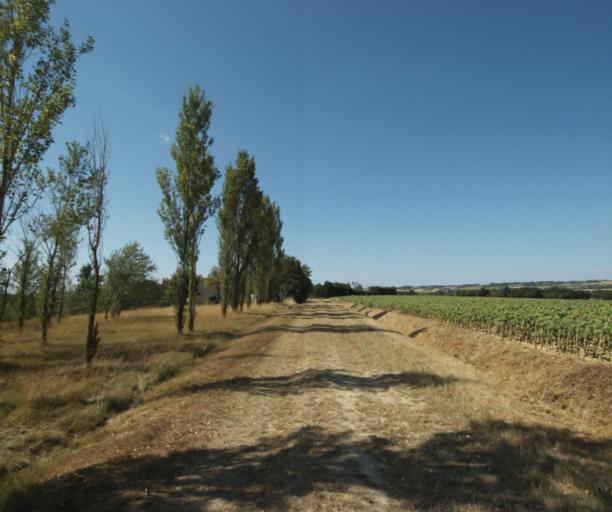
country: FR
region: Midi-Pyrenees
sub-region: Departement de la Haute-Garonne
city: Saint-Felix-Lauragais
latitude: 43.4780
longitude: 1.9088
